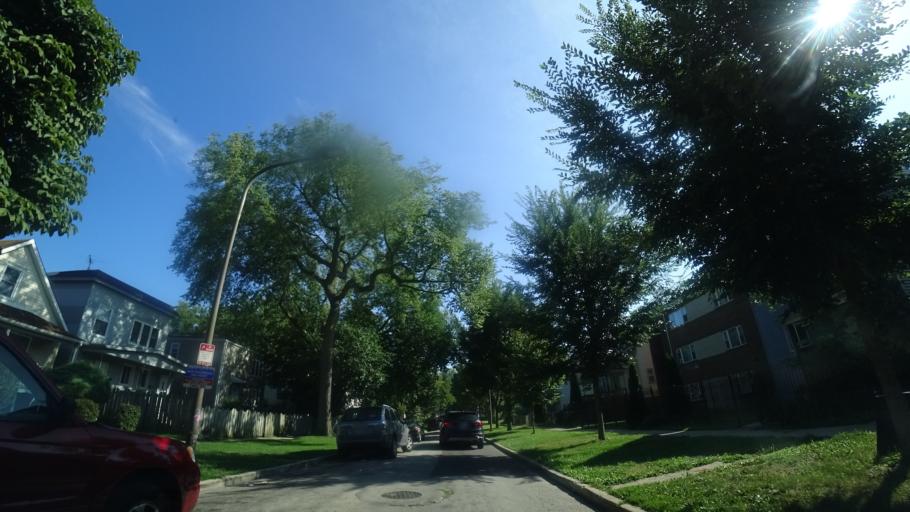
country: US
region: Illinois
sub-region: Cook County
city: Evanston
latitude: 42.0535
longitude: -87.6929
